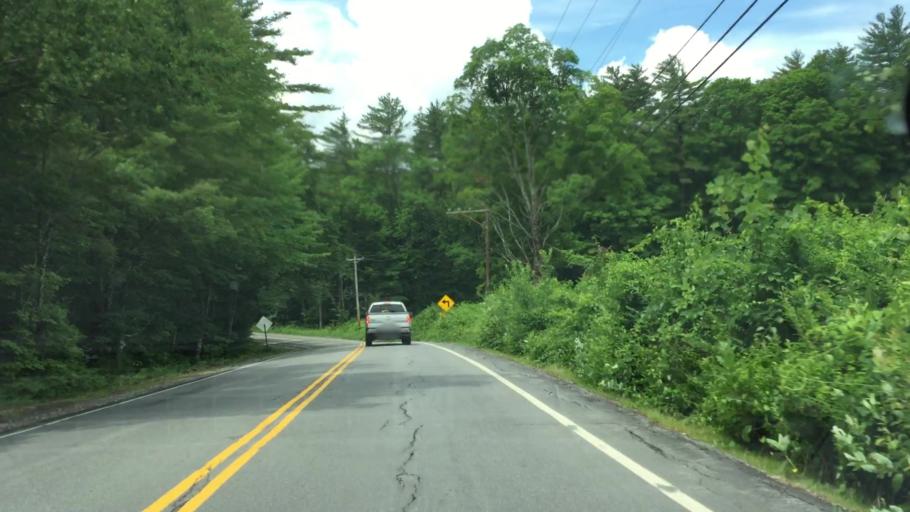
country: US
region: New Hampshire
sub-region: Grafton County
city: Holderness
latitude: 43.7474
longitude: -71.5605
